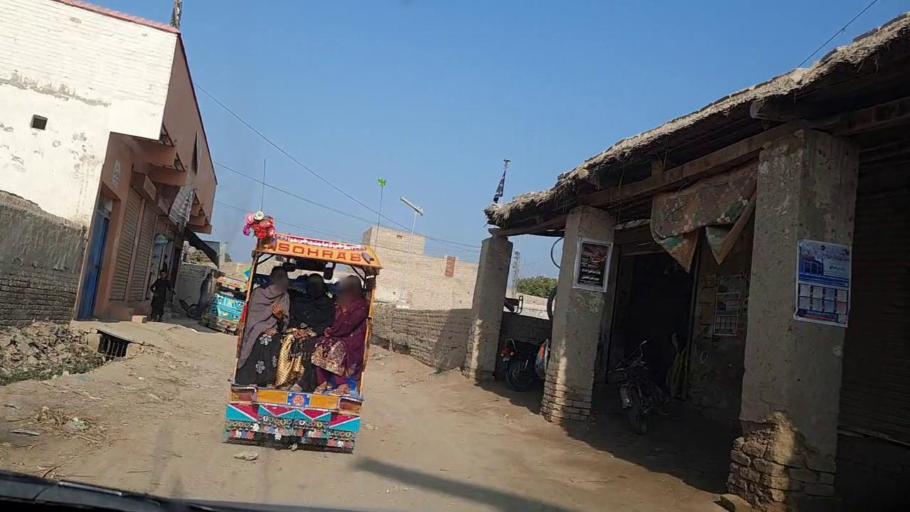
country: PK
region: Sindh
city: Moro
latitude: 26.7915
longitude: 67.9421
